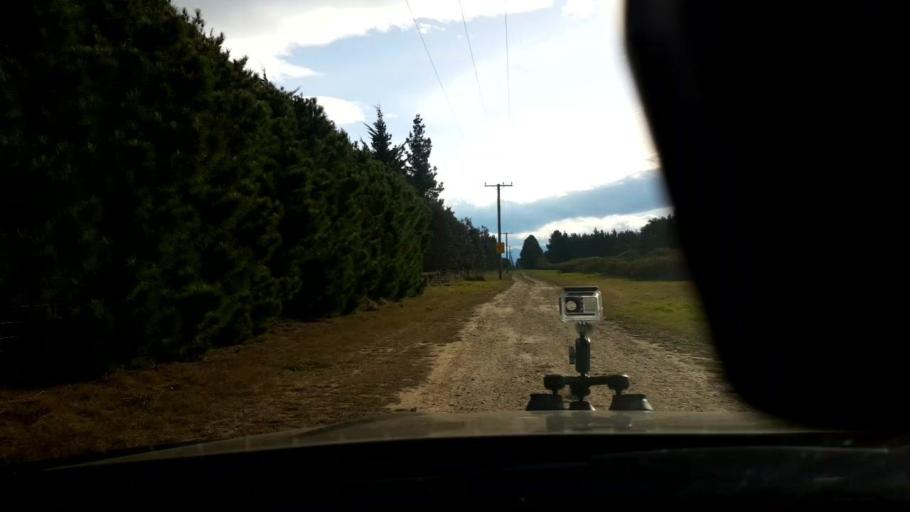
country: NZ
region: Canterbury
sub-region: Waimakariri District
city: Oxford
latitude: -43.3963
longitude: 172.3057
